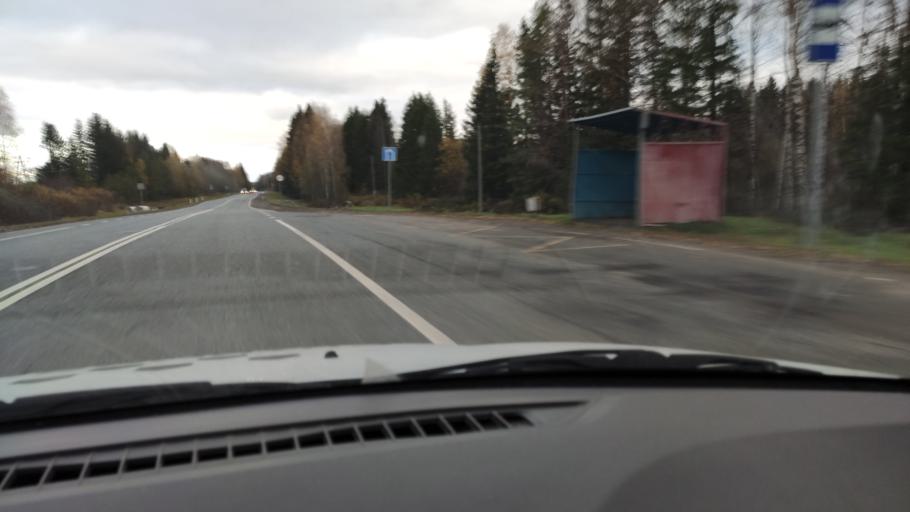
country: RU
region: Kirov
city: Belaya Kholunitsa
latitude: 58.8447
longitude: 50.7051
